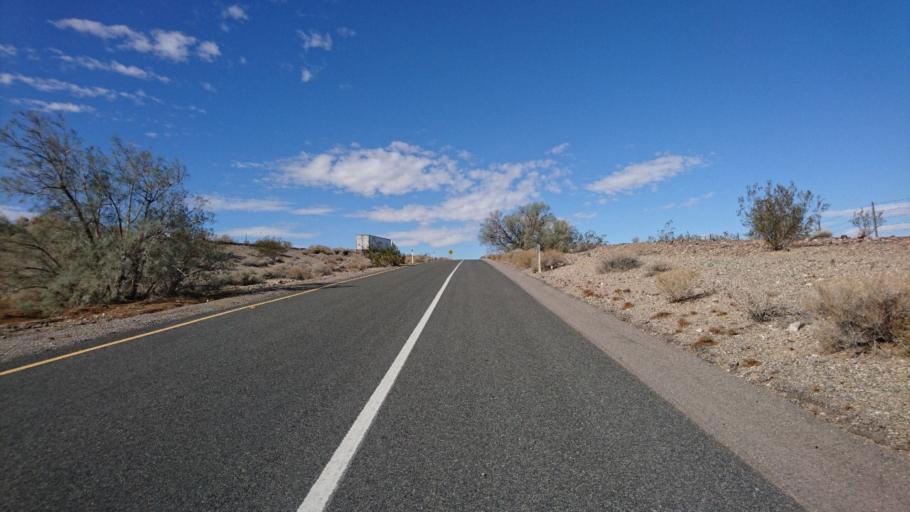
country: US
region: California
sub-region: San Bernardino County
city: Barstow
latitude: 34.8645
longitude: -116.9332
